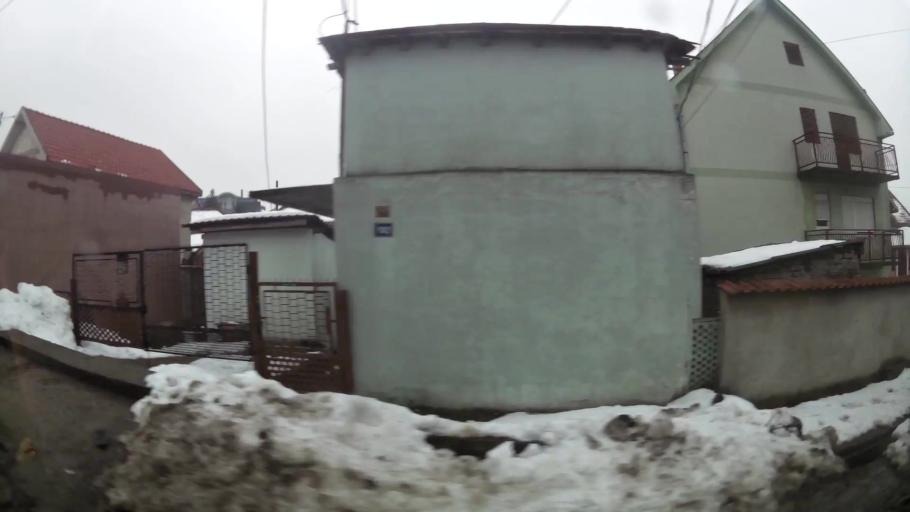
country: RS
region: Central Serbia
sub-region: Belgrade
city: Zvezdara
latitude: 44.7741
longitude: 20.5239
